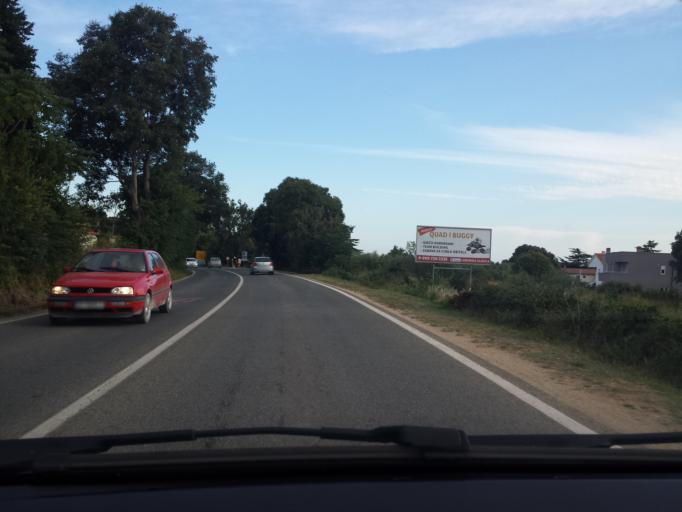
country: HR
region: Istarska
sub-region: Grad Pula
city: Pula
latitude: 44.8949
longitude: 13.8451
